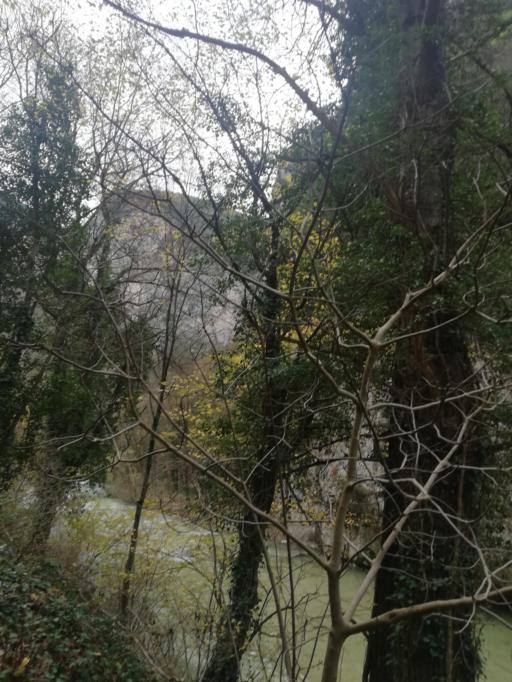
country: IT
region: The Marches
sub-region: Provincia di Ancona
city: Genga
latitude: 43.4051
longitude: 12.9468
